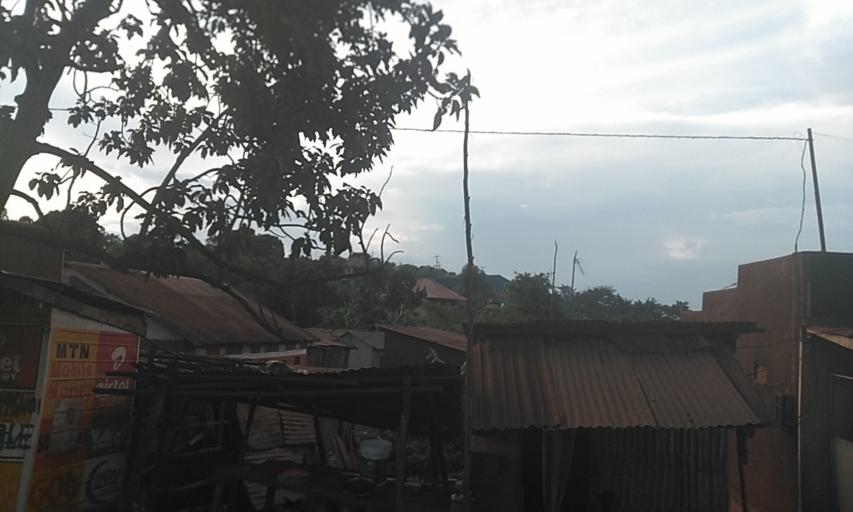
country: UG
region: Central Region
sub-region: Wakiso District
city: Kajansi
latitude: 0.2640
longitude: 32.5120
